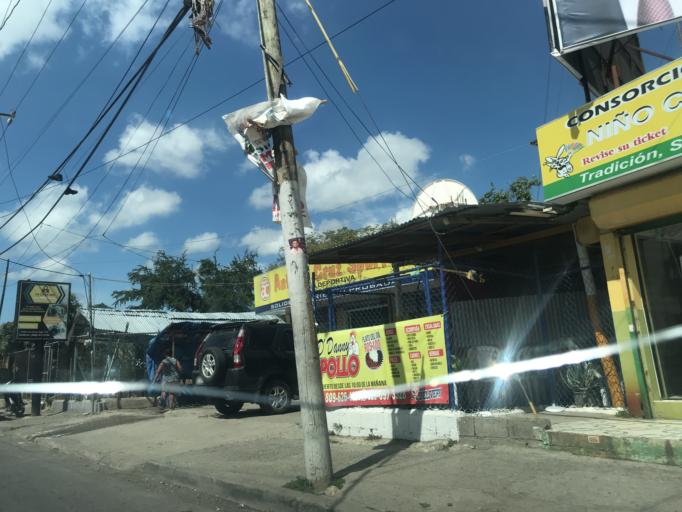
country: DO
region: Santiago
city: Palmar Arriba
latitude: 19.4938
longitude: -70.7410
